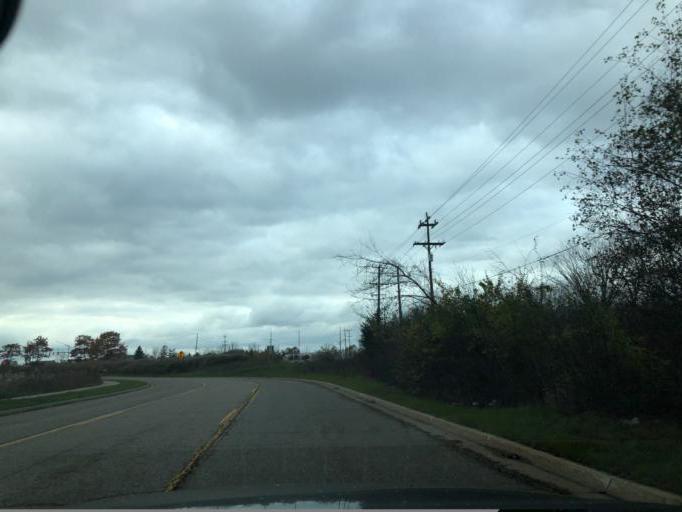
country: US
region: Michigan
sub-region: Washtenaw County
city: Ann Arbor
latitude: 42.2433
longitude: -83.7645
